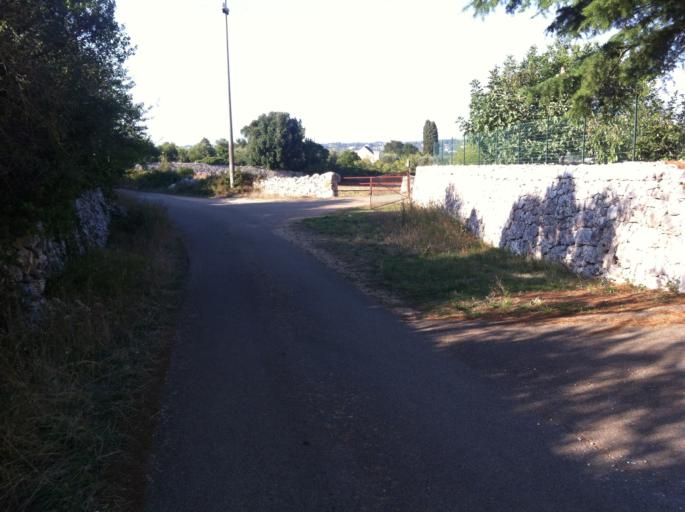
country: IT
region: Apulia
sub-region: Provincia di Bari
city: Noci
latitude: 40.8231
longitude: 17.1397
